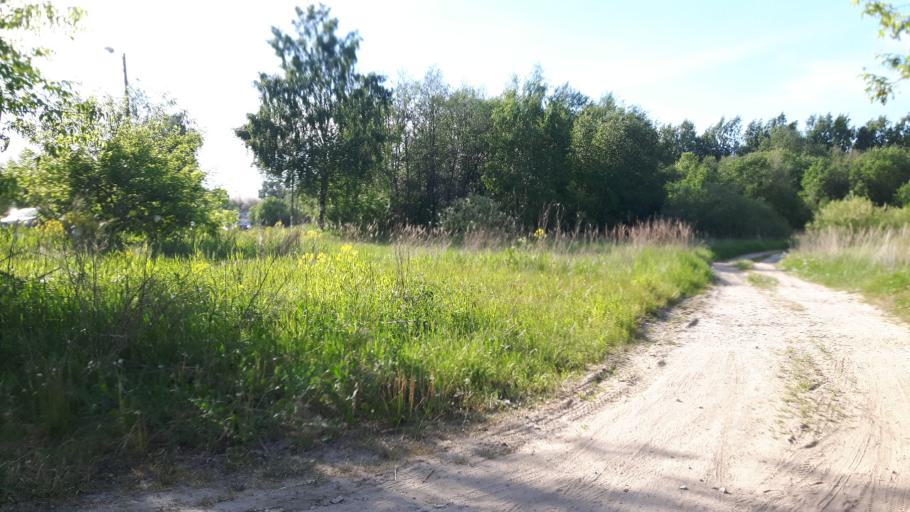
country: EE
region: Harju
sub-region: Tallinna linn
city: Kose
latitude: 59.4467
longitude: 24.9047
